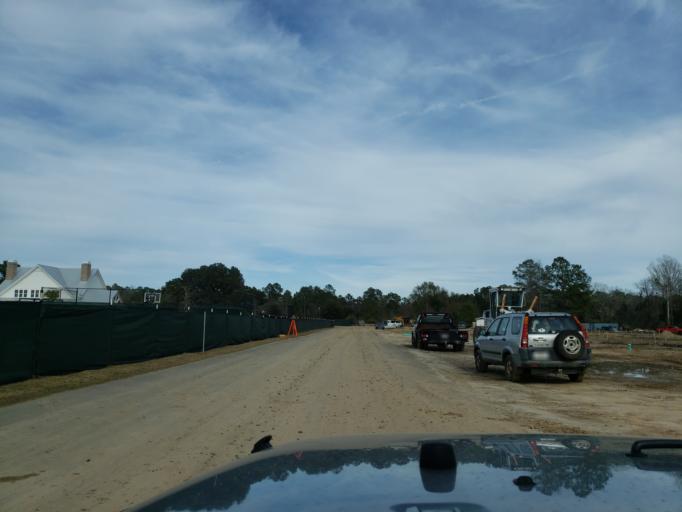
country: US
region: Georgia
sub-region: Bryan County
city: Richmond Hill
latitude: 32.0096
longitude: -81.2980
